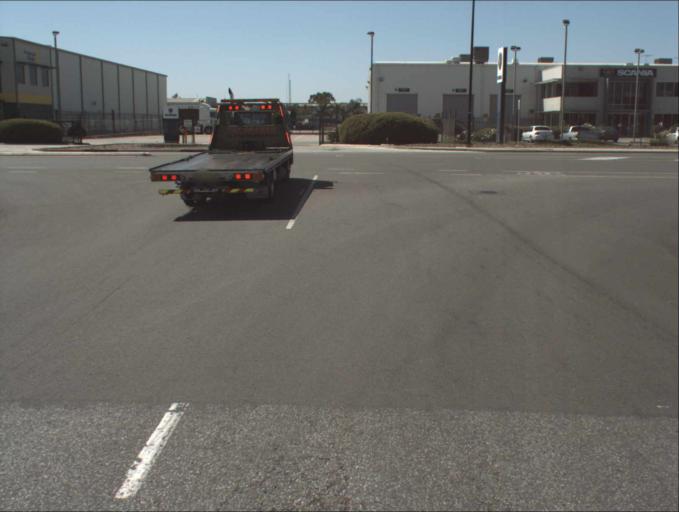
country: AU
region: South Australia
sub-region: Charles Sturt
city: Woodville North
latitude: -34.8410
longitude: 138.5624
